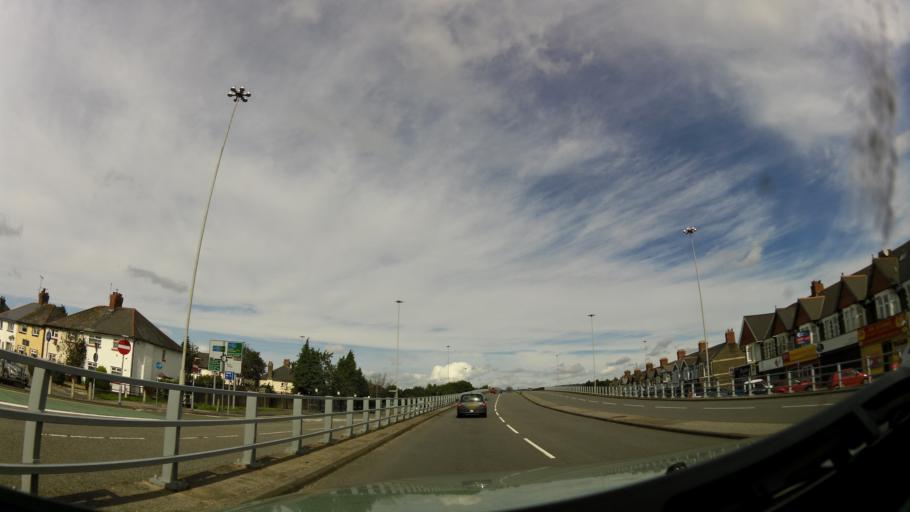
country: GB
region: Wales
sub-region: Cardiff
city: Cardiff
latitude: 51.5028
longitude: -3.1976
